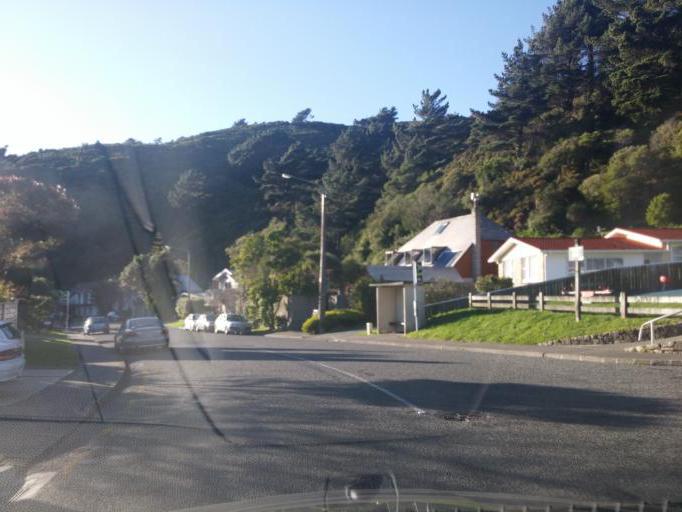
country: NZ
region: Wellington
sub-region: Wellington City
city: Kelburn
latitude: -41.2707
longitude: 174.7624
